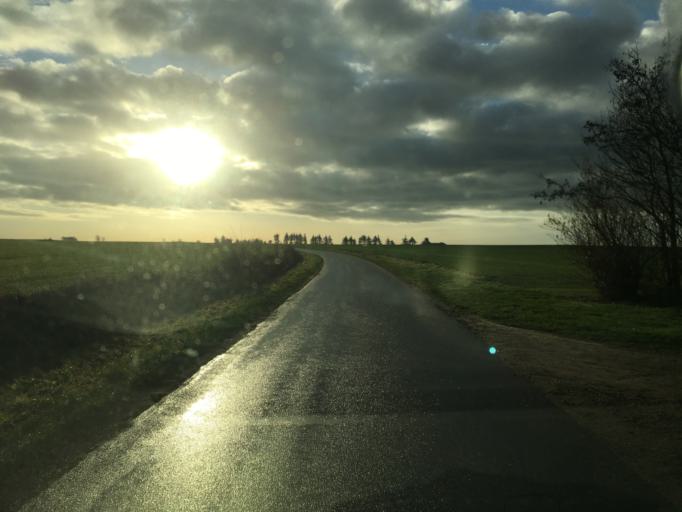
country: DK
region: South Denmark
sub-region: Tonder Kommune
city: Sherrebek
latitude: 55.1659
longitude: 8.8111
